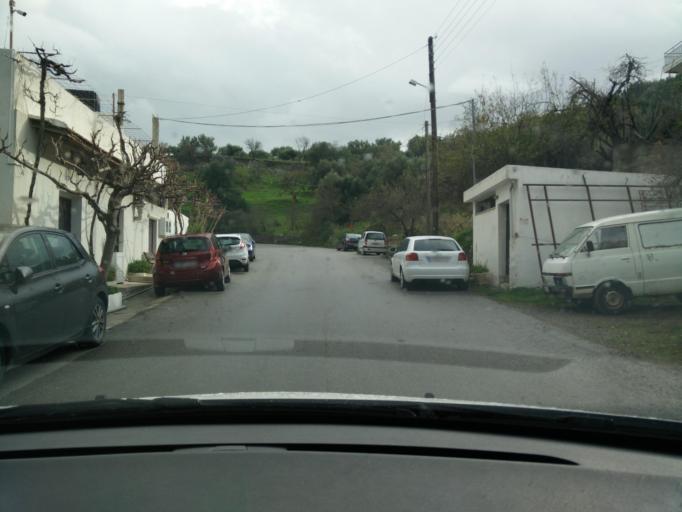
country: GR
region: Crete
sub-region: Nomos Lasithiou
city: Kritsa
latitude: 35.1554
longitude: 25.6435
